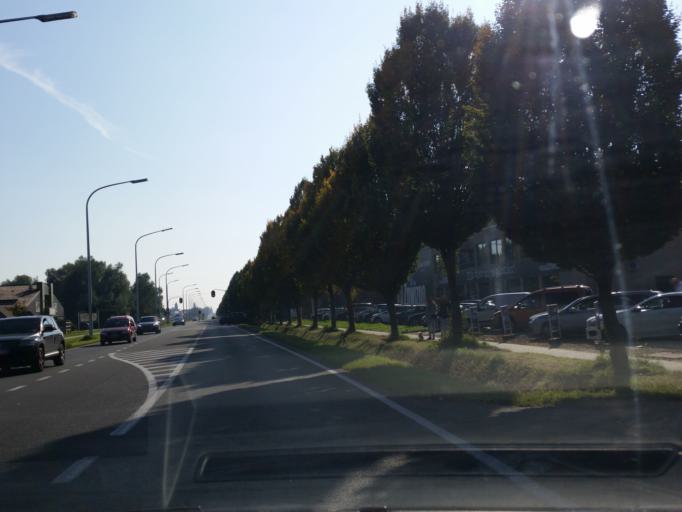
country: BE
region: Flanders
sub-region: Provincie Antwerpen
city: Kontich
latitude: 51.1230
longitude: 4.4499
